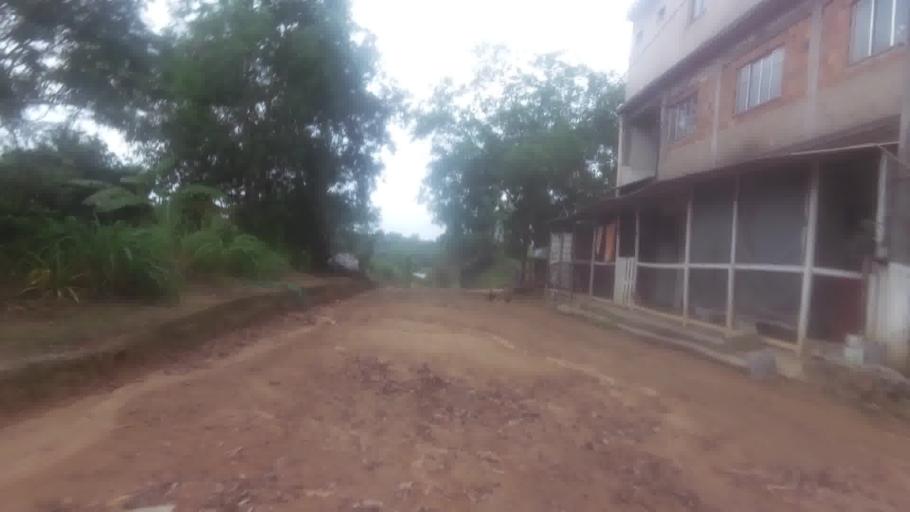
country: BR
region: Espirito Santo
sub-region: Piuma
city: Piuma
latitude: -20.7966
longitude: -40.5868
